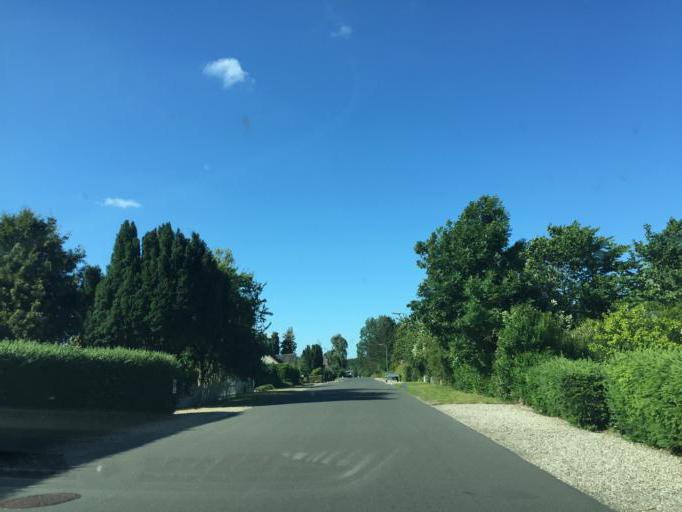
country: DK
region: South Denmark
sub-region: Odense Kommune
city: Hojby
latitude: 55.3408
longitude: 10.4383
